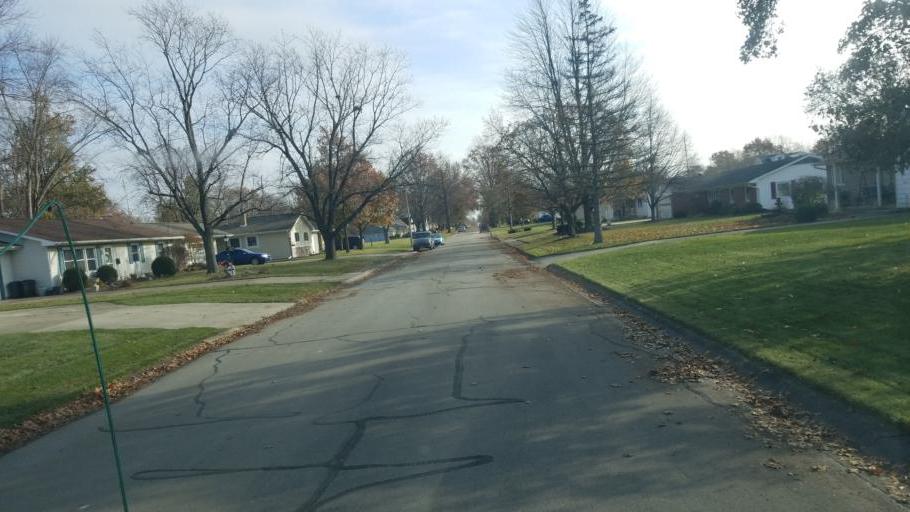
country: US
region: Indiana
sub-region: Adams County
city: Berne
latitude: 40.6584
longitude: -84.9625
